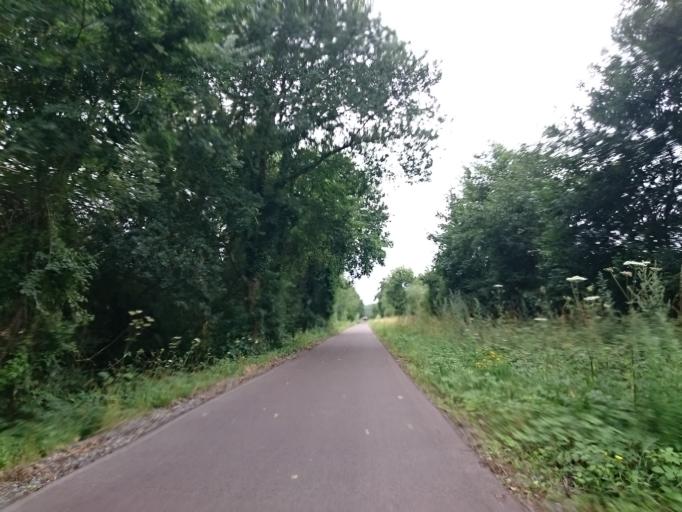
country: FR
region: Lower Normandy
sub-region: Departement du Calvados
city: Louvigny
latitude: 49.1377
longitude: -0.3953
